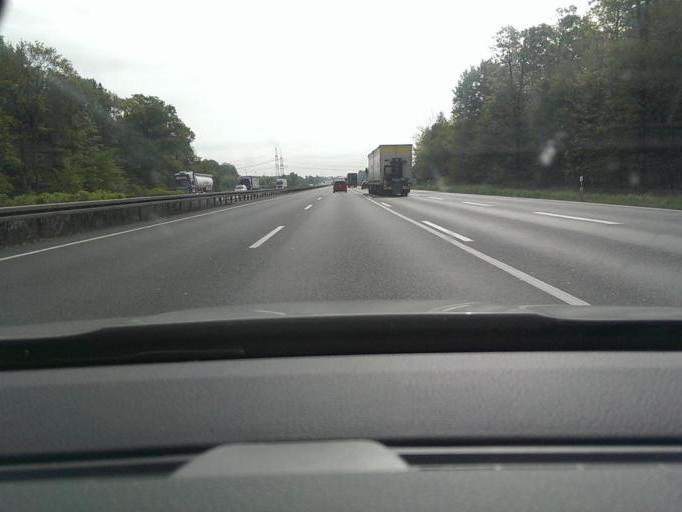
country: DE
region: Lower Saxony
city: Wendeburg
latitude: 52.3399
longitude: 10.3488
